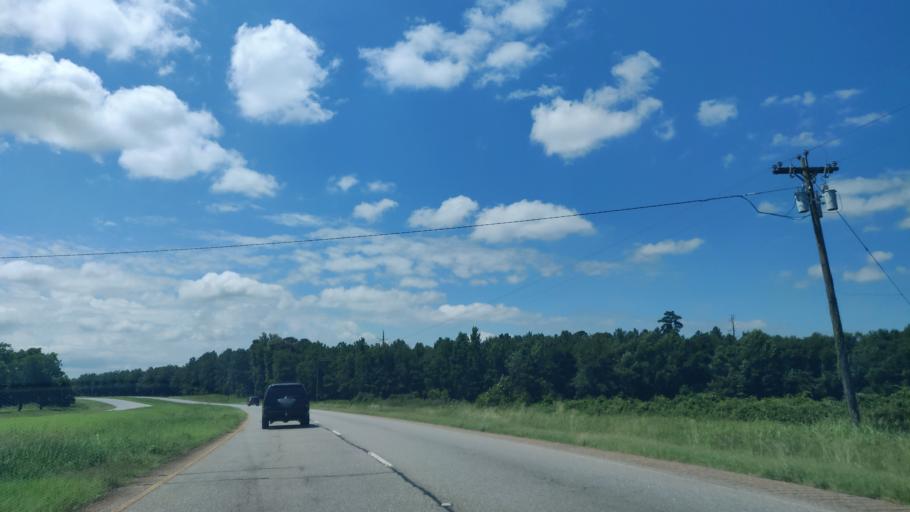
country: US
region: Georgia
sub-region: Stewart County
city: Richland
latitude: 32.0397
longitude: -84.6780
